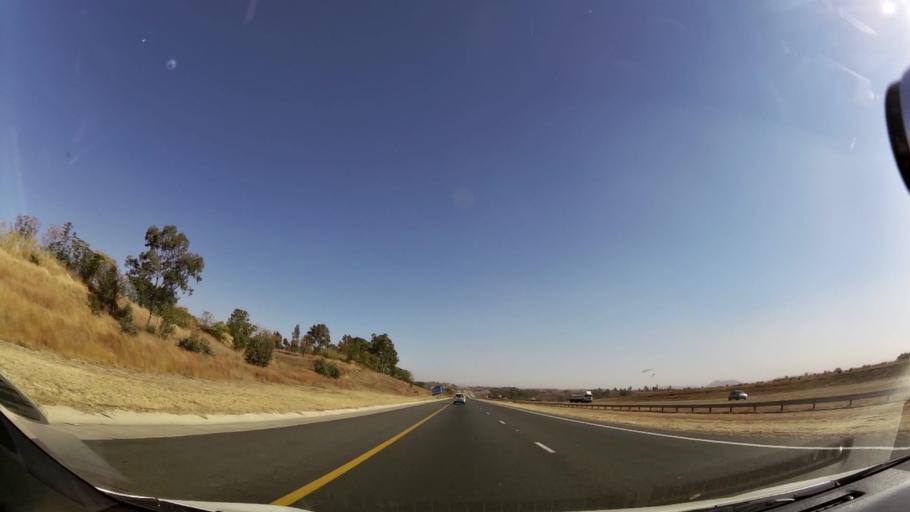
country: ZA
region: Gauteng
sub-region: City of Johannesburg Metropolitan Municipality
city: Diepsloot
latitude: -25.9740
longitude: 27.9396
